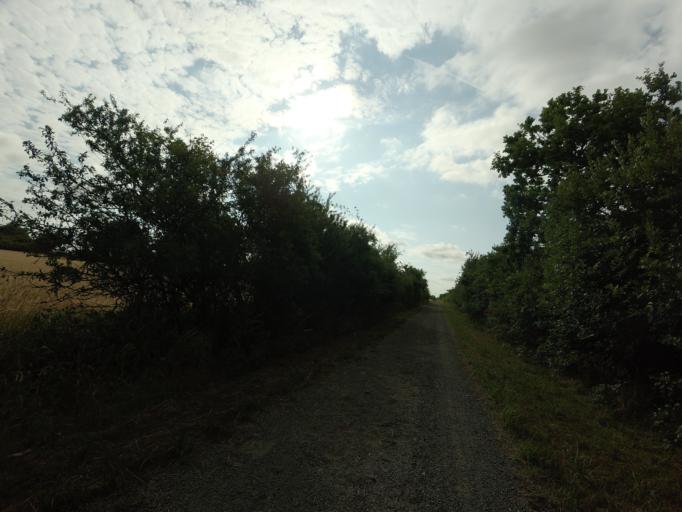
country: SE
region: Skane
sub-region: Helsingborg
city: Odakra
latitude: 56.1634
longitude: 12.7379
